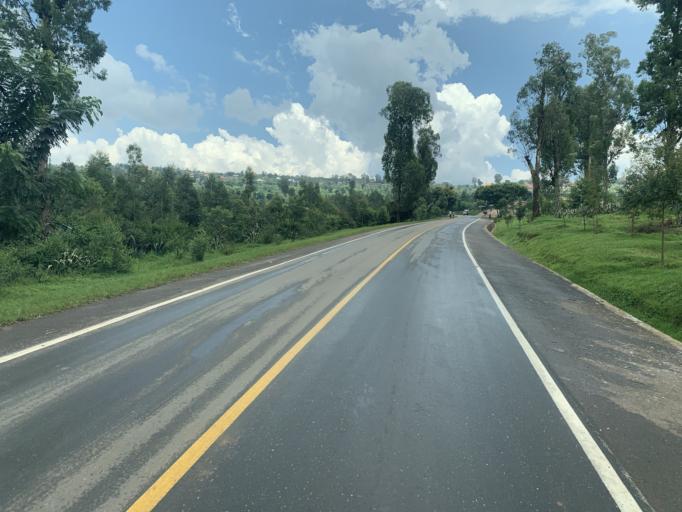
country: RW
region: Southern Province
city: Gitarama
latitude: -2.0067
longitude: 29.8961
